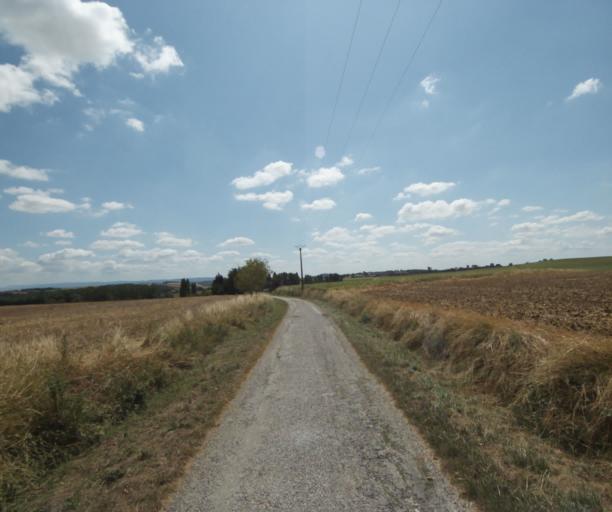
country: FR
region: Midi-Pyrenees
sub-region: Departement de la Haute-Garonne
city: Auriac-sur-Vendinelle
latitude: 43.4705
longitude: 1.8358
